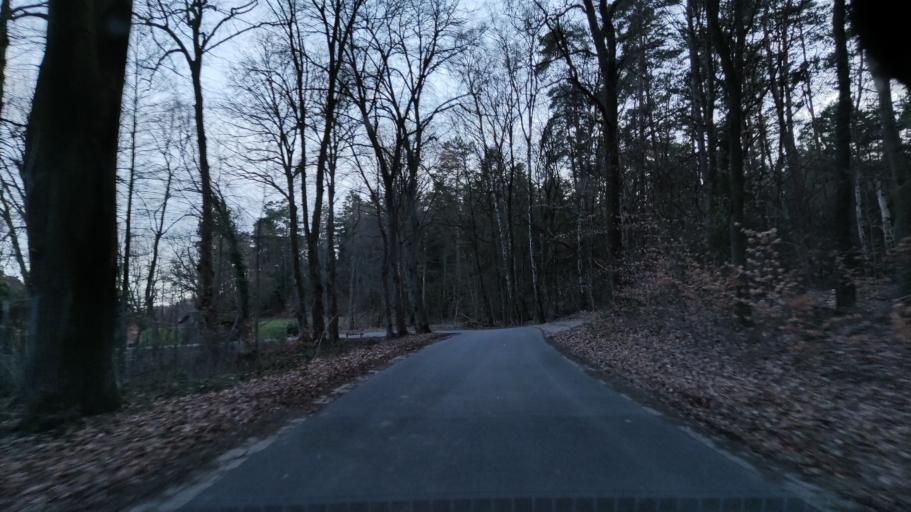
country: DE
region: Lower Saxony
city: Thomasburg
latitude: 53.2024
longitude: 10.6780
